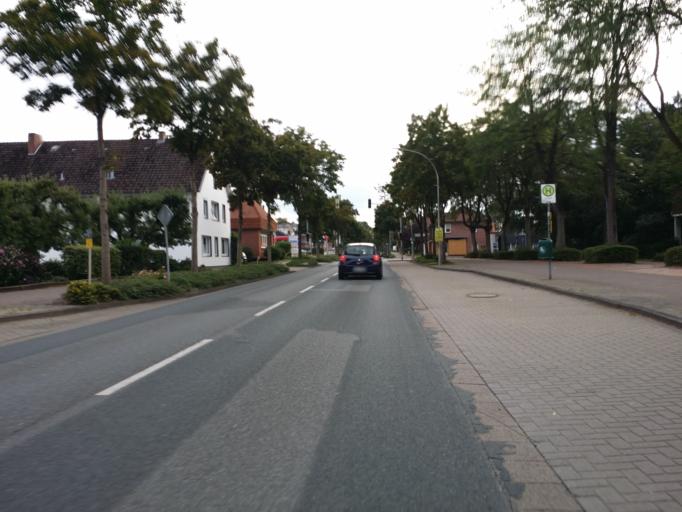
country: DE
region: Lower Saxony
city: Bremervorde
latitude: 53.4793
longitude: 9.1398
